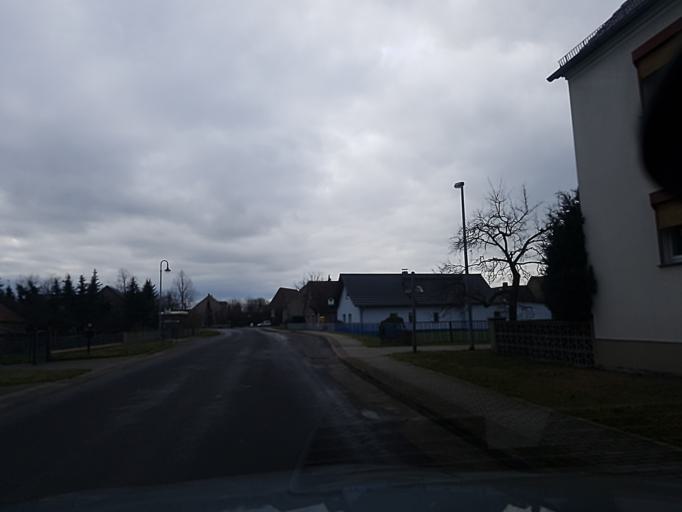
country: DE
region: Brandenburg
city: Falkenberg
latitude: 51.5295
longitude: 13.2988
